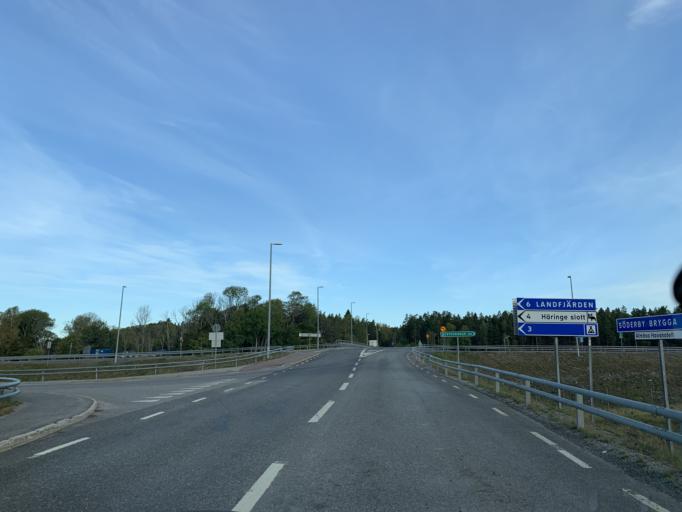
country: SE
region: Stockholm
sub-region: Haninge Kommun
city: Jordbro
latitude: 59.0671
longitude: 18.0644
